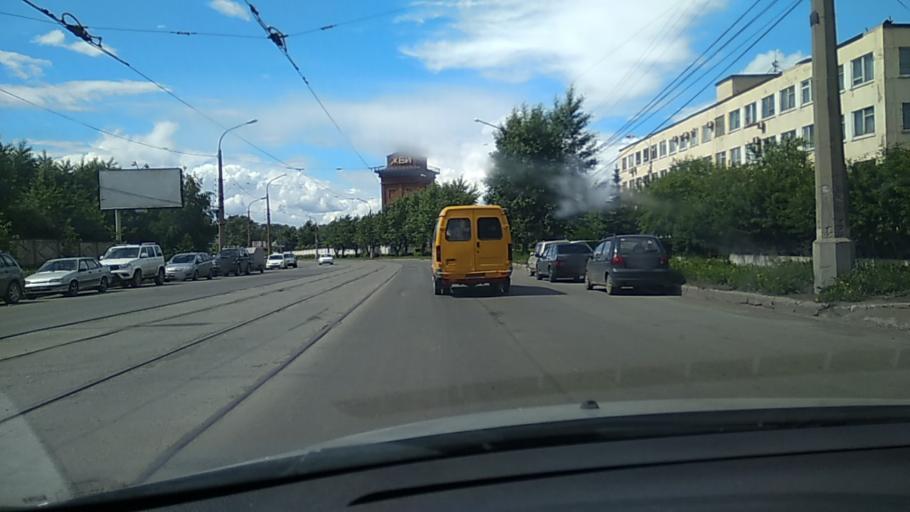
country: RU
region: Sverdlovsk
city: Nizhniy Tagil
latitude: 57.9293
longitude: 60.0068
